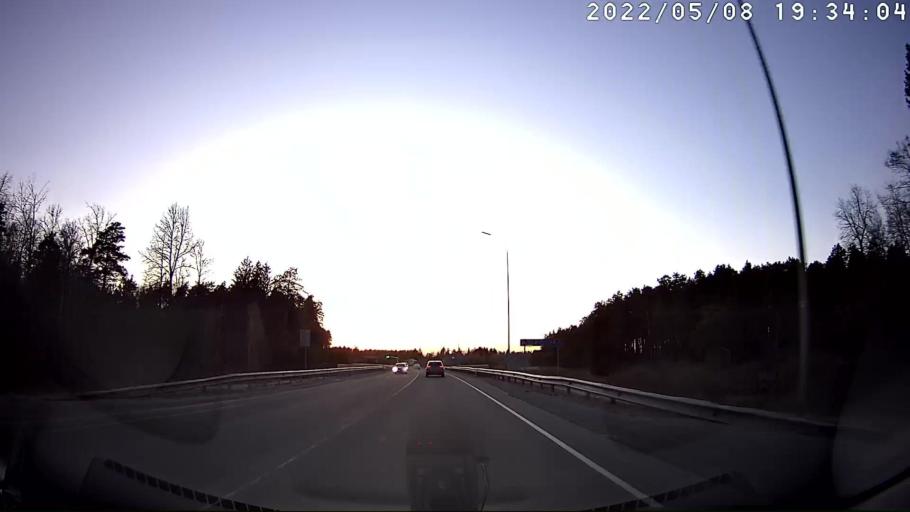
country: RU
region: Mariy-El
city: Yoshkar-Ola
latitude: 56.5388
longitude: 47.9838
